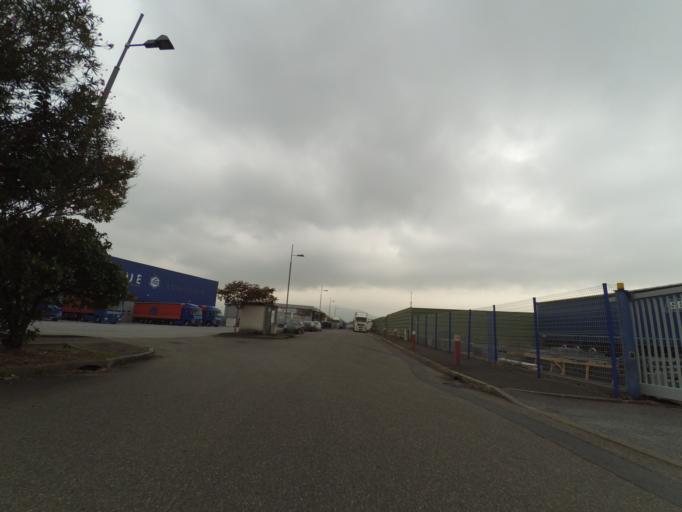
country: ES
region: Basque Country
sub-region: Provincia de Guipuzcoa
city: Irun
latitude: 43.3466
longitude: -1.7740
